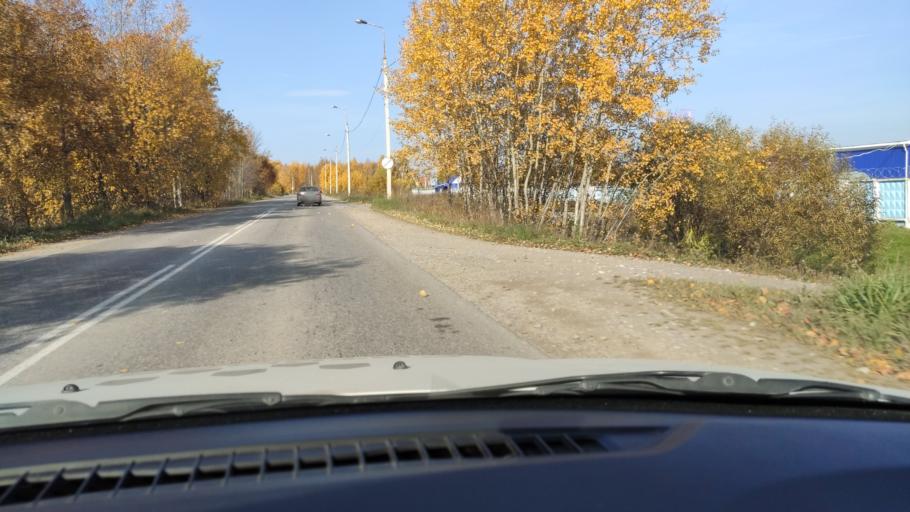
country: RU
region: Perm
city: Novyye Lyady
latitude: 58.0463
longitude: 56.5908
